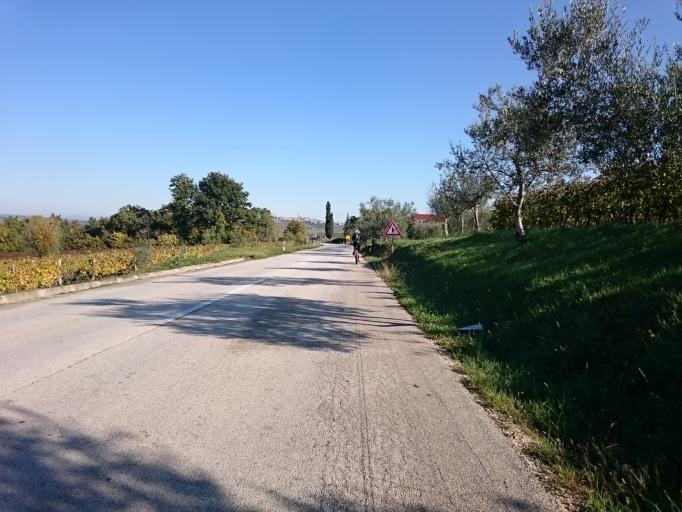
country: HR
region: Istarska
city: Buje
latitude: 45.3857
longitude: 13.6320
